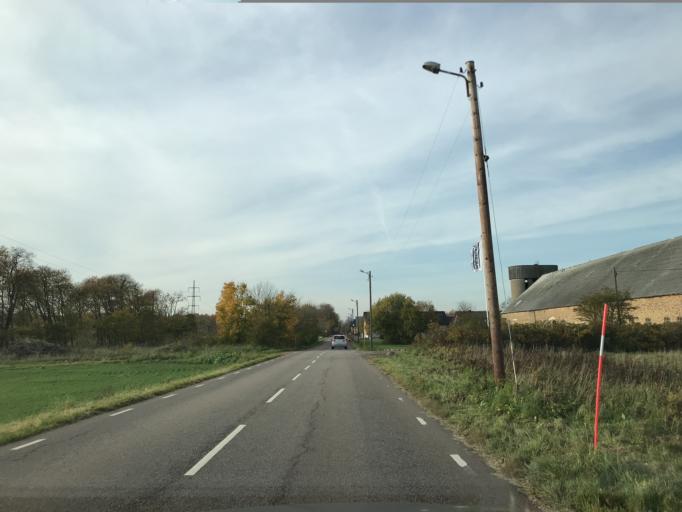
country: SE
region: Skane
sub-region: Helsingborg
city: Hyllinge
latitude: 56.1006
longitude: 12.8742
